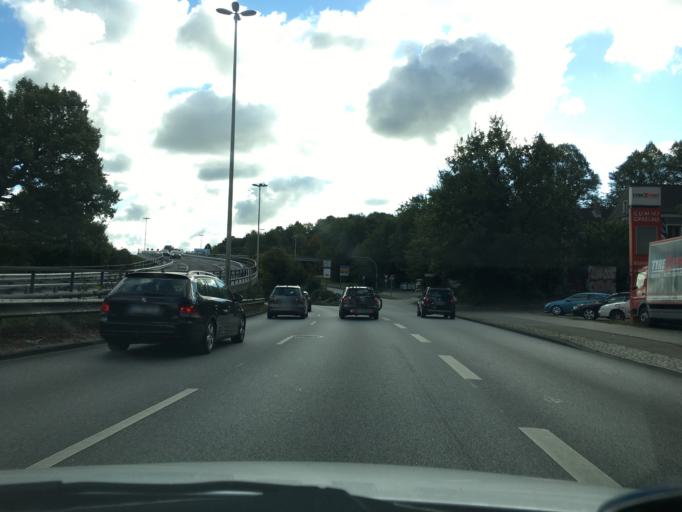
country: DE
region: Schleswig-Holstein
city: Kiel
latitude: 54.3036
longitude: 10.1243
